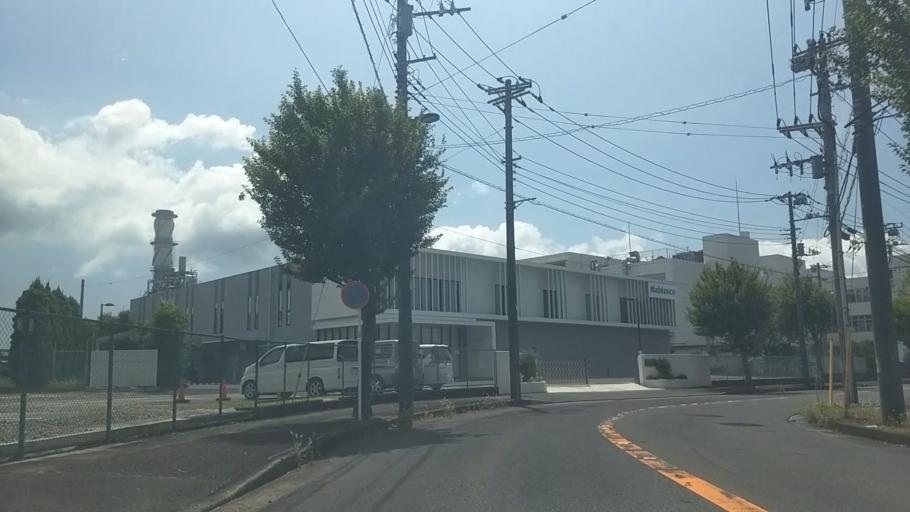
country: JP
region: Kanagawa
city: Yokosuka
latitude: 35.3125
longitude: 139.6419
